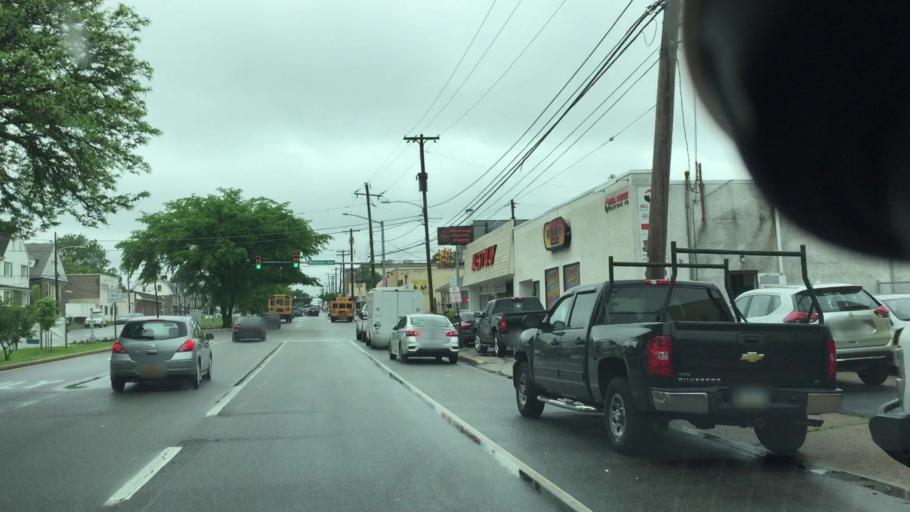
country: US
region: Pennsylvania
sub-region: Delaware County
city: Drexel Hill
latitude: 39.9679
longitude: -75.2904
